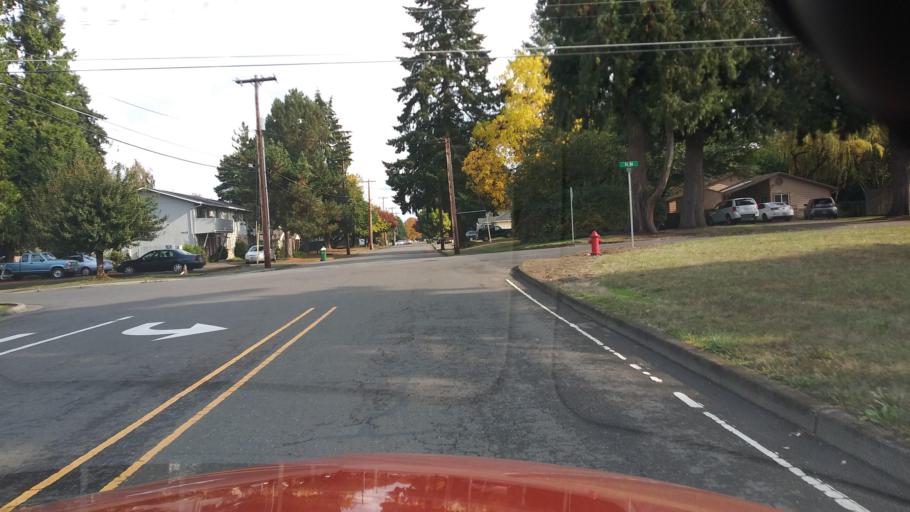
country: US
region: Oregon
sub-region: Washington County
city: Cornelius
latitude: 45.5183
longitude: -123.0840
